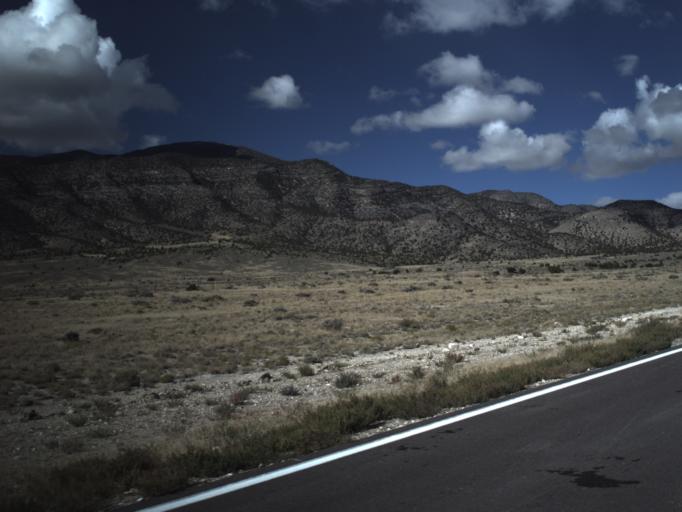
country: US
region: Utah
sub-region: Beaver County
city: Milford
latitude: 38.4995
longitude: -113.4960
